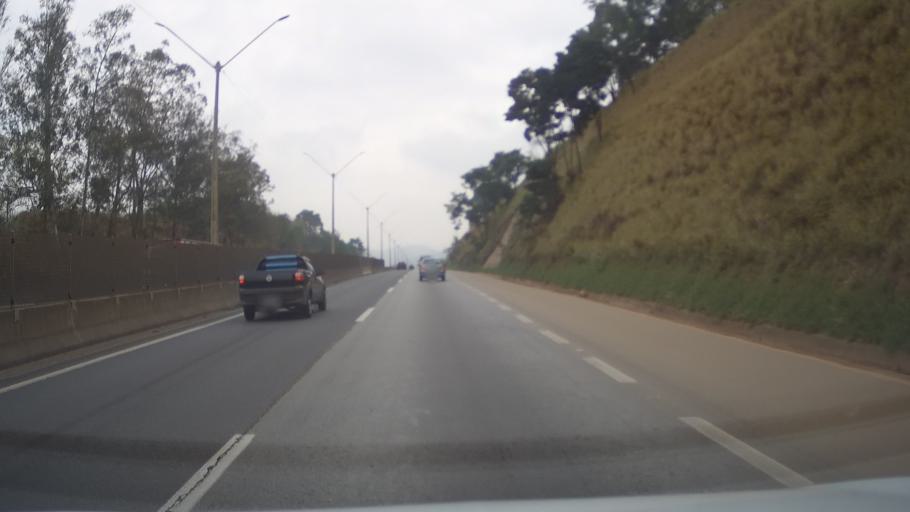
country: BR
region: Sao Paulo
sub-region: Atibaia
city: Atibaia
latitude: -23.0509
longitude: -46.5662
